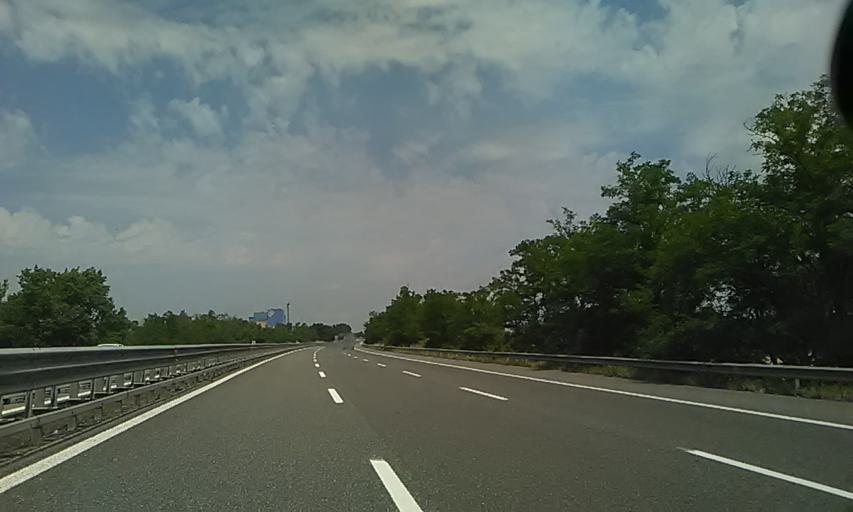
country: IT
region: Piedmont
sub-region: Provincia di Alessandria
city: Capriata d'Orba
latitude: 44.7137
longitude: 8.6667
